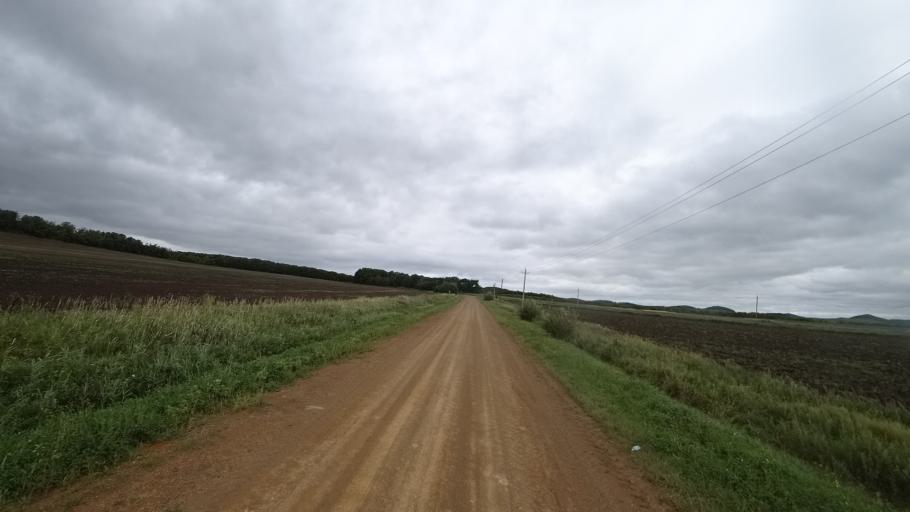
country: RU
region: Primorskiy
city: Chernigovka
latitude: 44.4479
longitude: 132.5970
